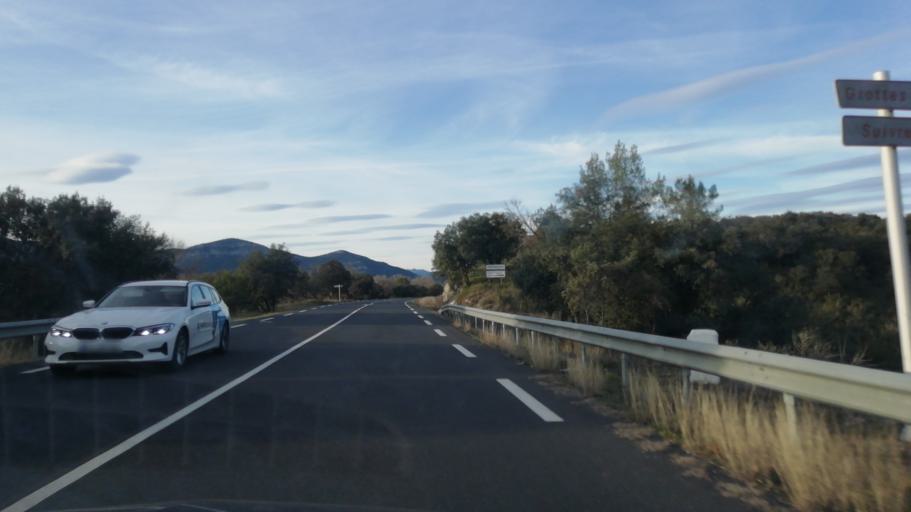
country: FR
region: Languedoc-Roussillon
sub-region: Departement du Gard
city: Quissac
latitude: 43.8872
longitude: 4.0162
